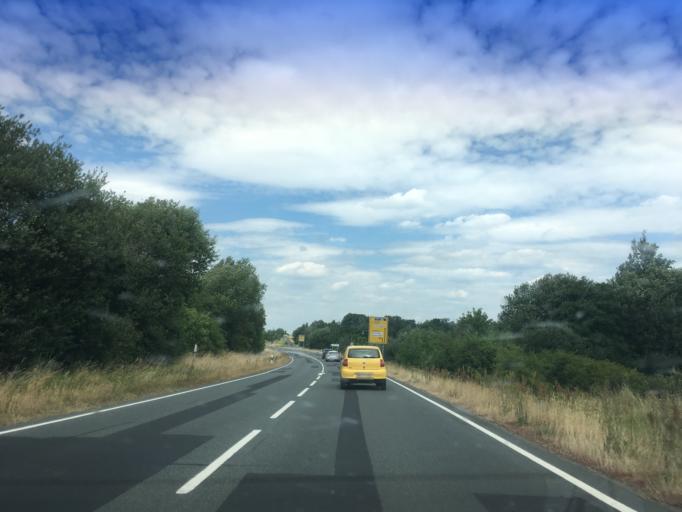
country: DE
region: Saxony
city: Goerlitz
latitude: 51.1601
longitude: 14.9559
